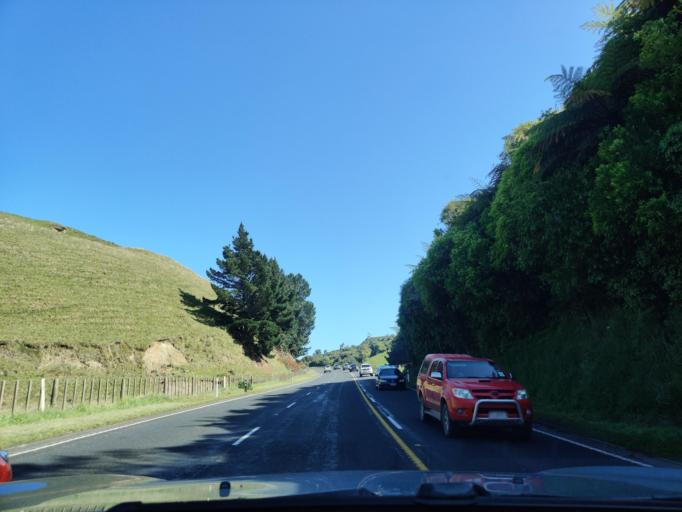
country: NZ
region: Manawatu-Wanganui
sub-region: Wanganui District
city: Wanganui
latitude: -40.0317
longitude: 175.2050
